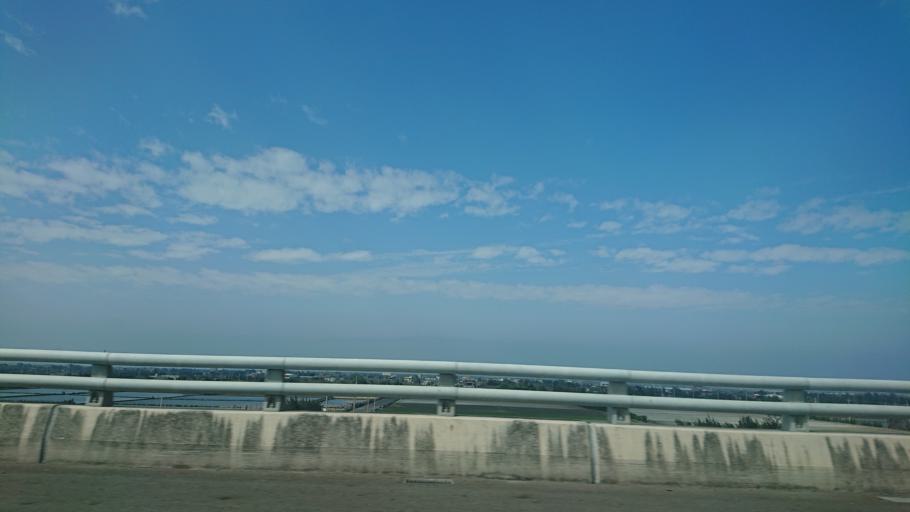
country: TW
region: Taiwan
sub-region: Yunlin
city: Douliu
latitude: 23.8458
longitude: 120.2937
